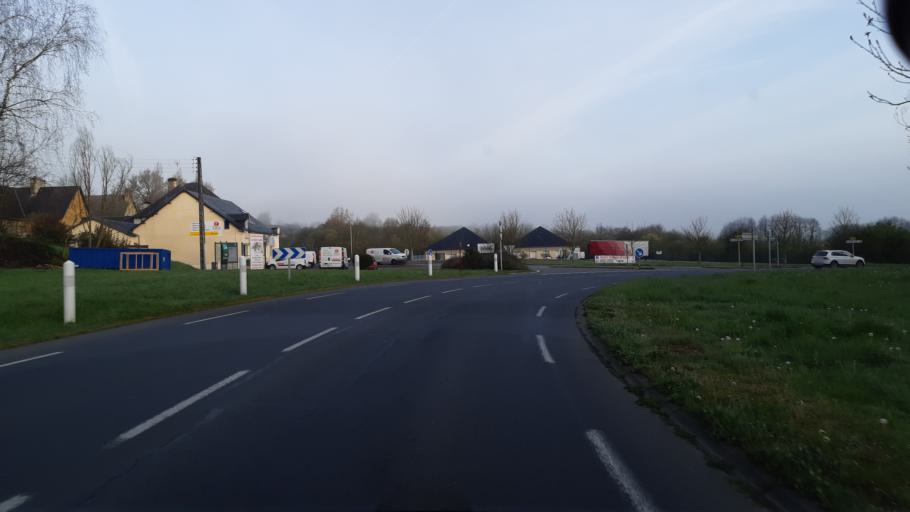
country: FR
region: Lower Normandy
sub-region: Departement de la Manche
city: Agneaux
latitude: 49.0891
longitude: -1.1188
